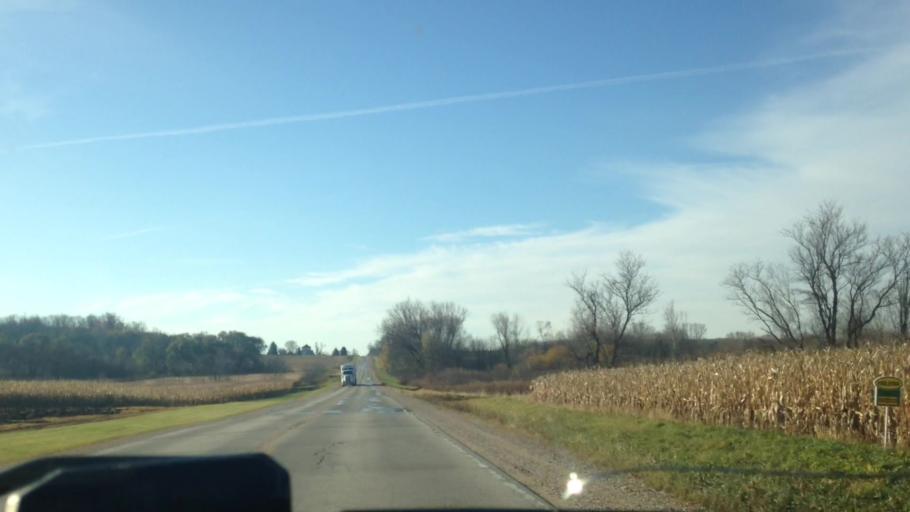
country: US
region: Wisconsin
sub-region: Dodge County
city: Mayville
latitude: 43.4508
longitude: -88.5002
